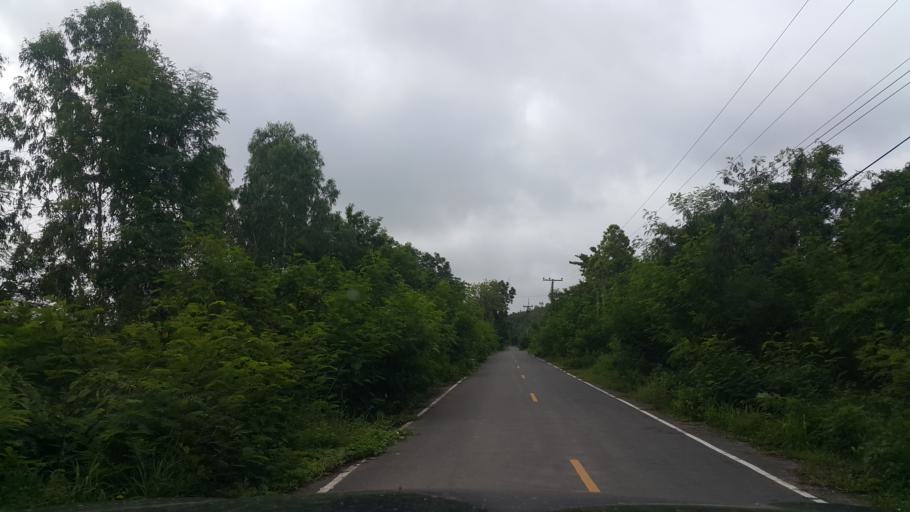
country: TH
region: Sukhothai
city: Sawankhalok
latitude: 17.3073
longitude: 99.7074
